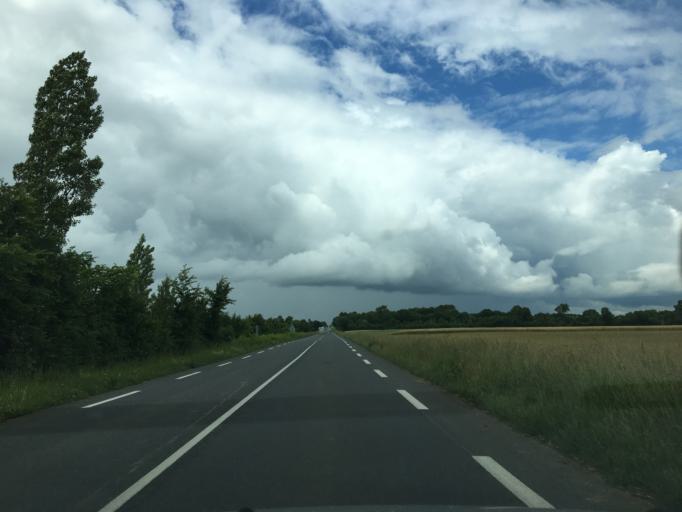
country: FR
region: Poitou-Charentes
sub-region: Departement de la Charente-Maritime
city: Saint-Jean-d'Angely
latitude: 46.0624
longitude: -0.5085
